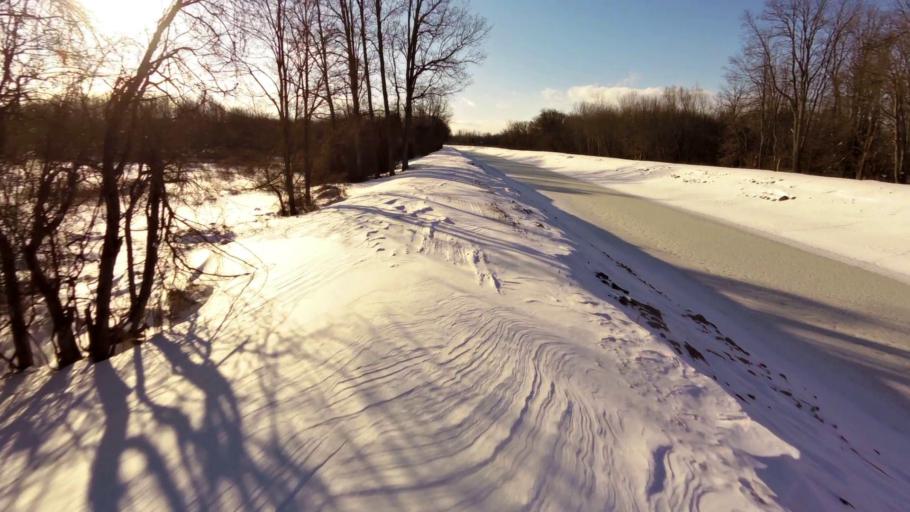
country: US
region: New York
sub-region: Orleans County
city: Albion
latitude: 43.2547
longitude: -78.2220
